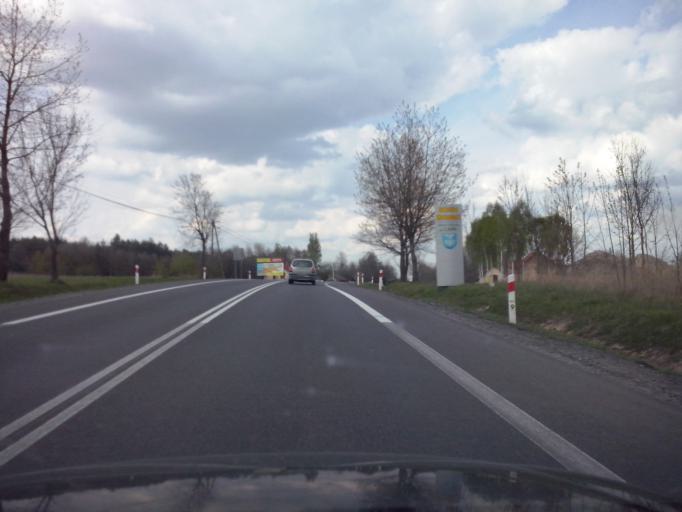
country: PL
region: Subcarpathian Voivodeship
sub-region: Powiat rzeszowski
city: Sokolow Malopolski
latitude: 50.2172
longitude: 22.1086
